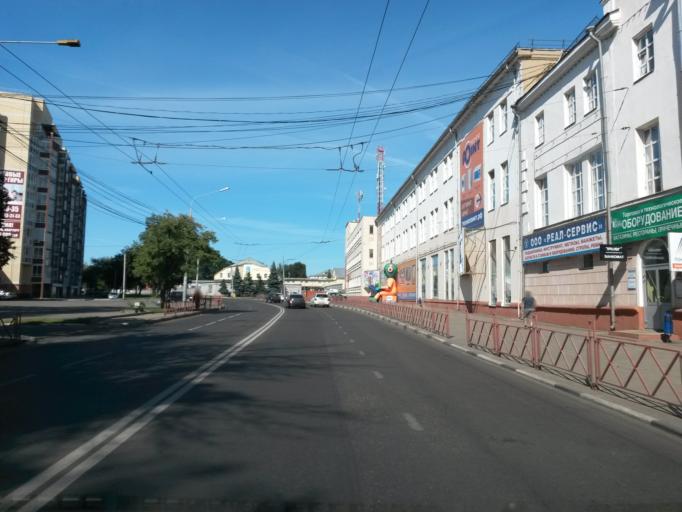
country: RU
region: Jaroslavl
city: Yaroslavl
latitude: 57.6402
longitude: 39.8834
